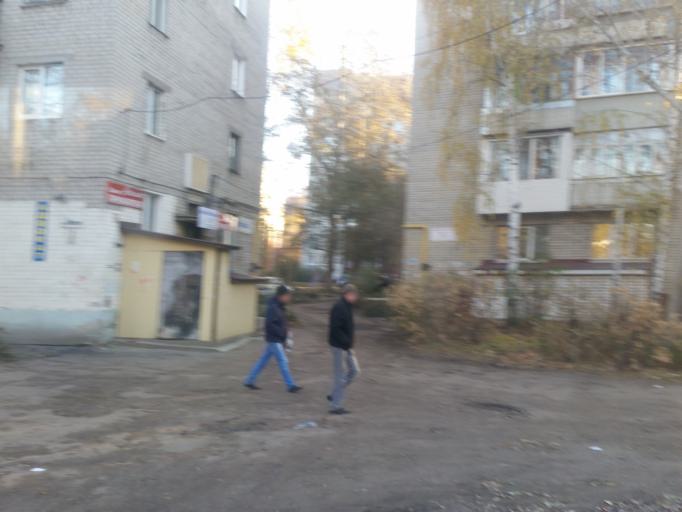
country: RU
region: Ulyanovsk
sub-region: Ulyanovskiy Rayon
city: Ulyanovsk
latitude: 54.3249
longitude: 48.3862
